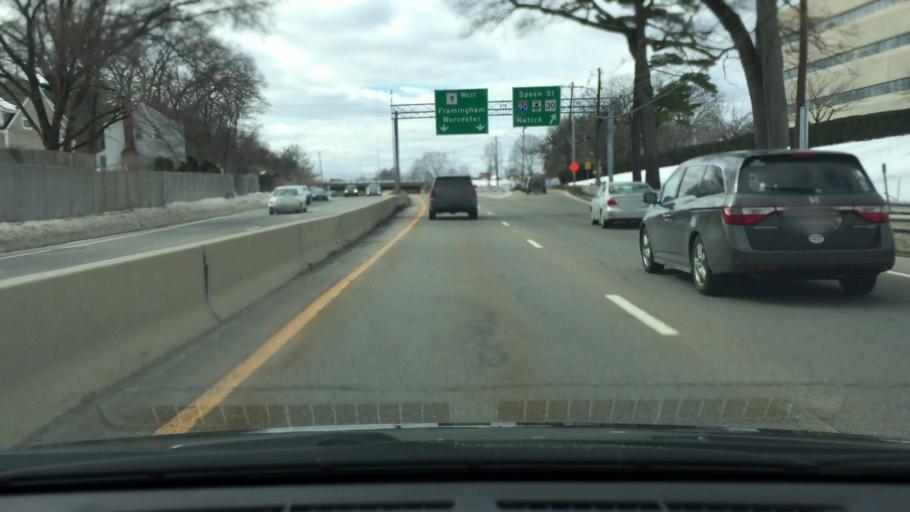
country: US
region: Massachusetts
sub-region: Middlesex County
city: Cochituate
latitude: 42.2990
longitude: -71.3733
